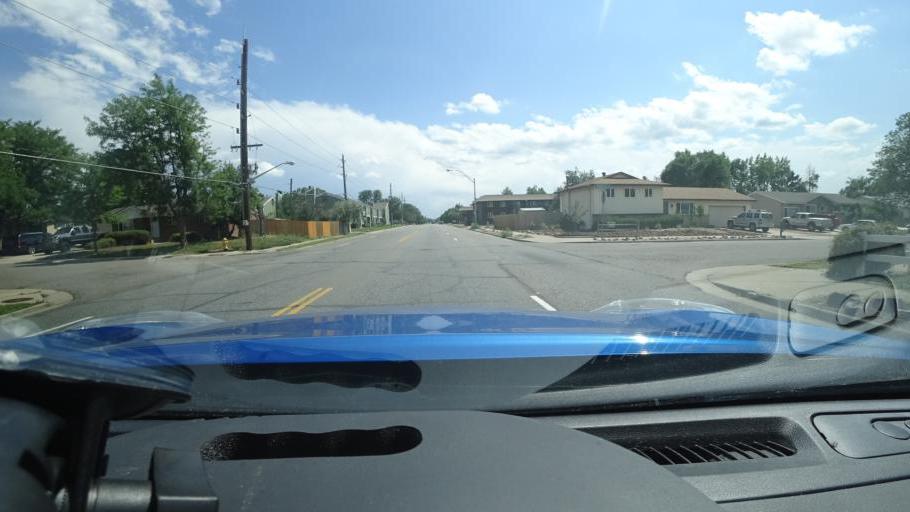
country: US
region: Colorado
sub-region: Adams County
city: Aurora
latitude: 39.7020
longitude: -104.8472
